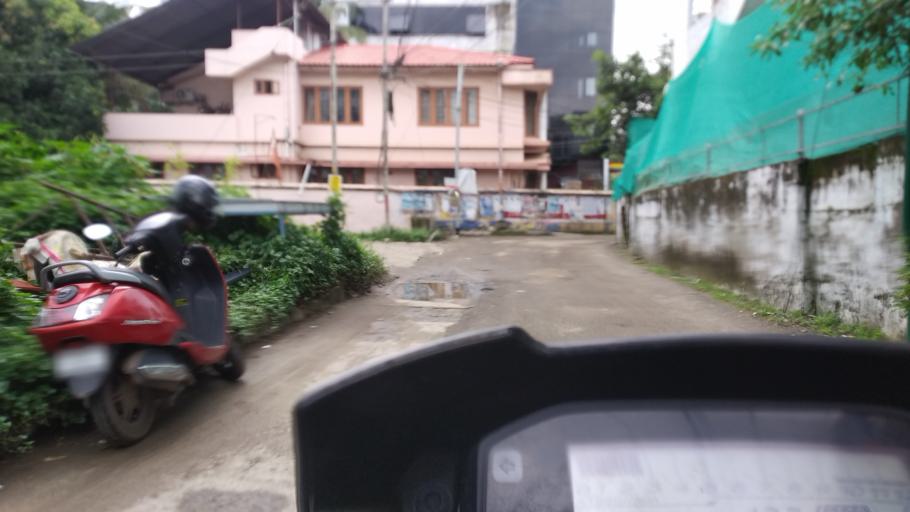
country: IN
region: Kerala
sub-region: Ernakulam
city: Cochin
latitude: 9.9729
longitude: 76.3103
